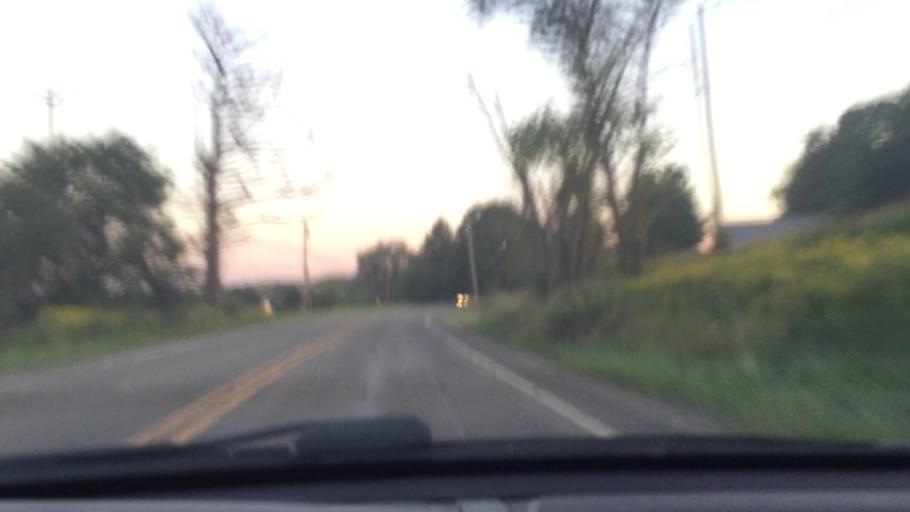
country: US
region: Pennsylvania
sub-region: Butler County
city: Slippery Rock
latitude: 41.1003
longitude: -80.0519
